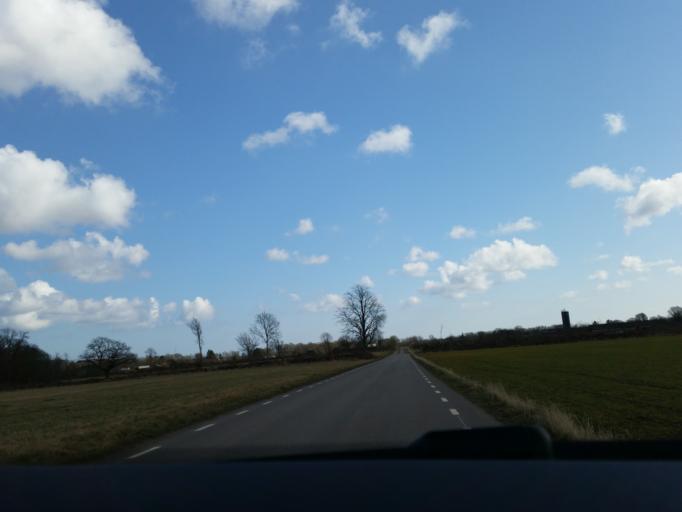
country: SE
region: Kalmar
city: Faerjestaden
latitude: 56.6887
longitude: 16.5688
